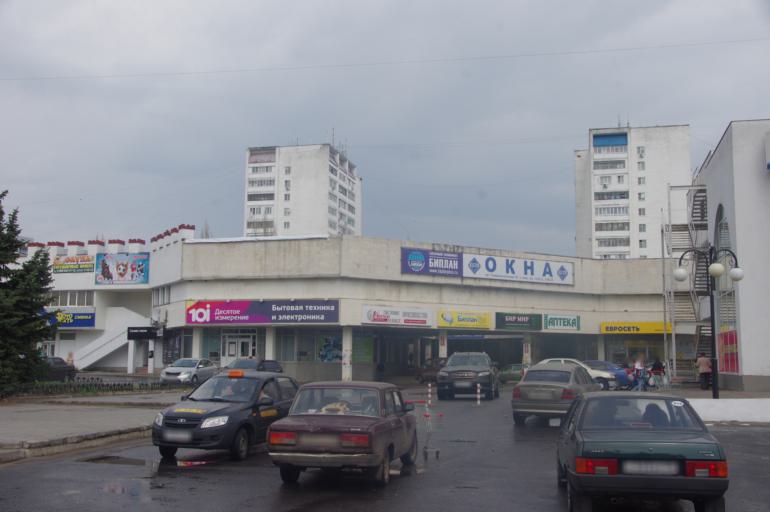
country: RU
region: Kursk
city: Kurchatov
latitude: 51.6596
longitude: 35.6578
